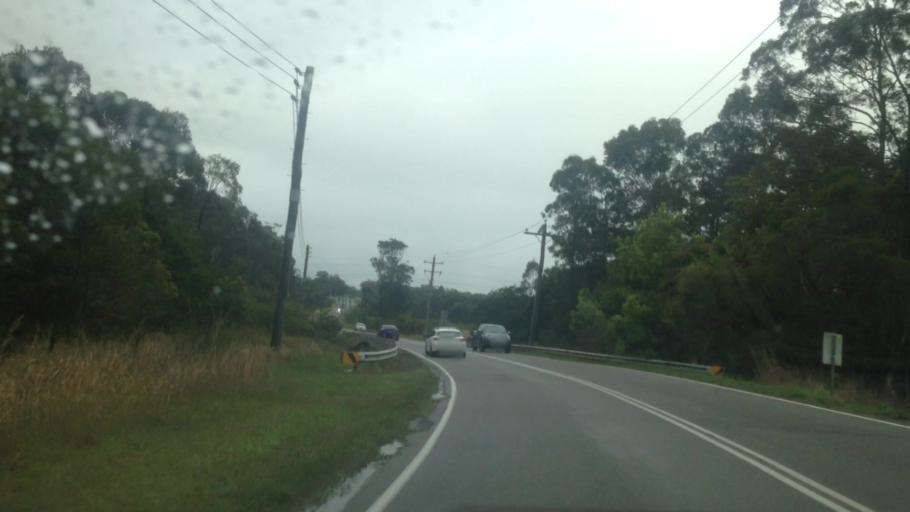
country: AU
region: New South Wales
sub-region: Wyong Shire
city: Charmhaven
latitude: -33.1642
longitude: 151.4784
